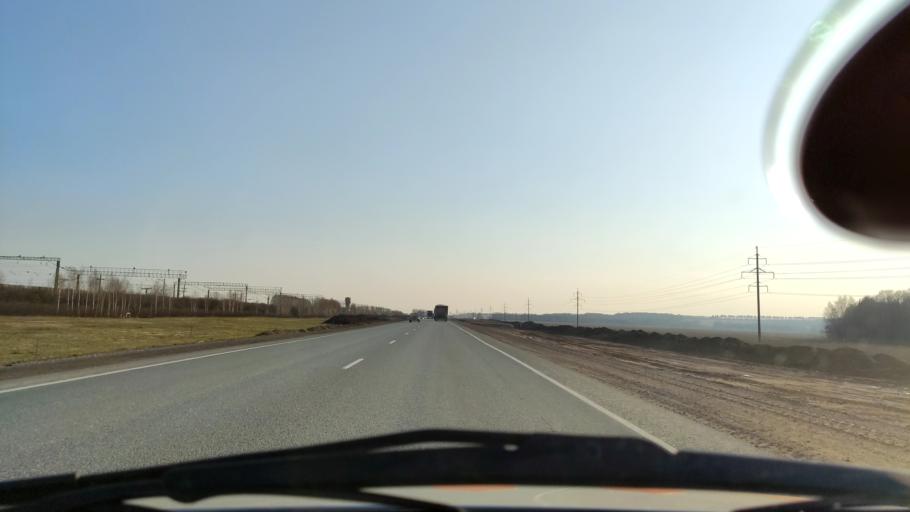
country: RU
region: Bashkortostan
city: Kabakovo
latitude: 54.7145
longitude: 56.2308
